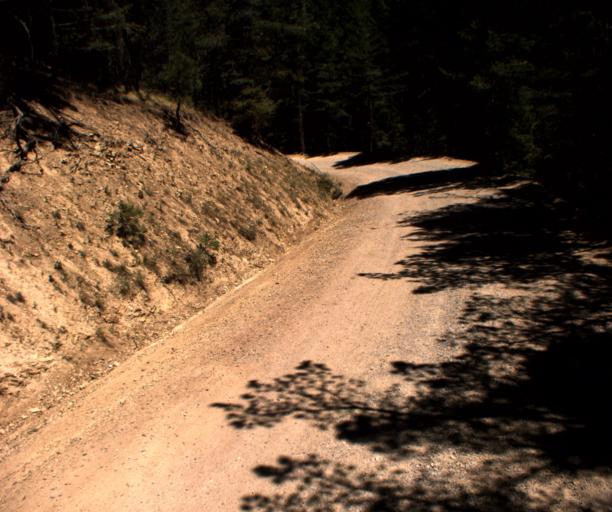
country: US
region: Arizona
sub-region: Graham County
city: Swift Trail Junction
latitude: 32.6782
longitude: -109.8877
